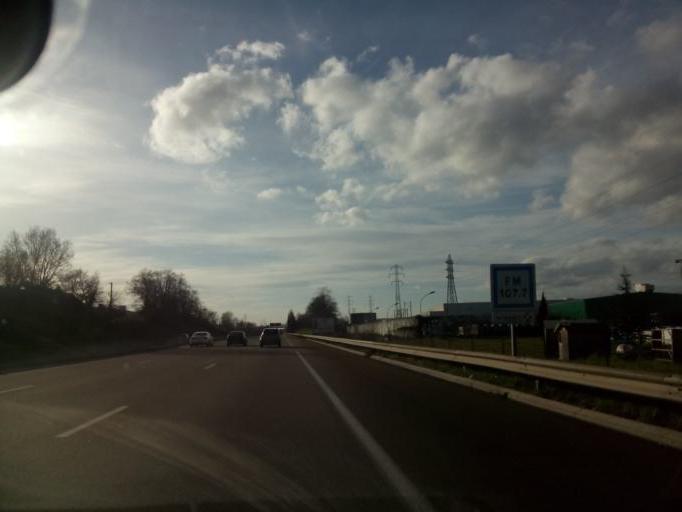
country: FR
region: Rhone-Alpes
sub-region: Departement de l'Isere
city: Salaise-sur-Sanne
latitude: 45.3455
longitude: 4.8071
